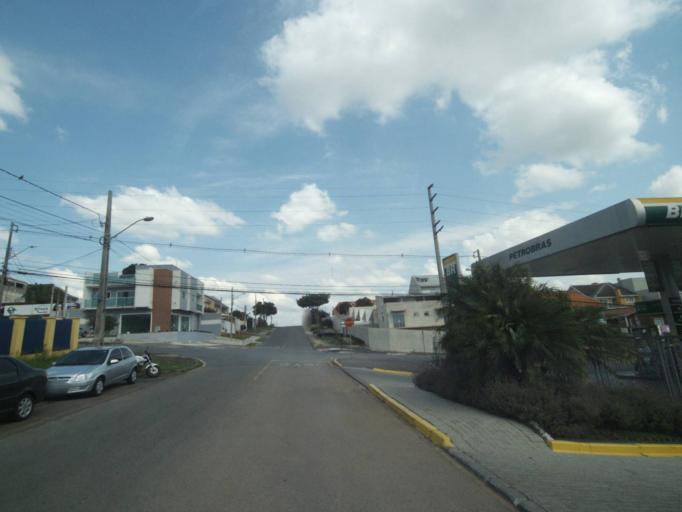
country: BR
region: Parana
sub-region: Pinhais
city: Pinhais
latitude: -25.4082
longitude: -49.2122
